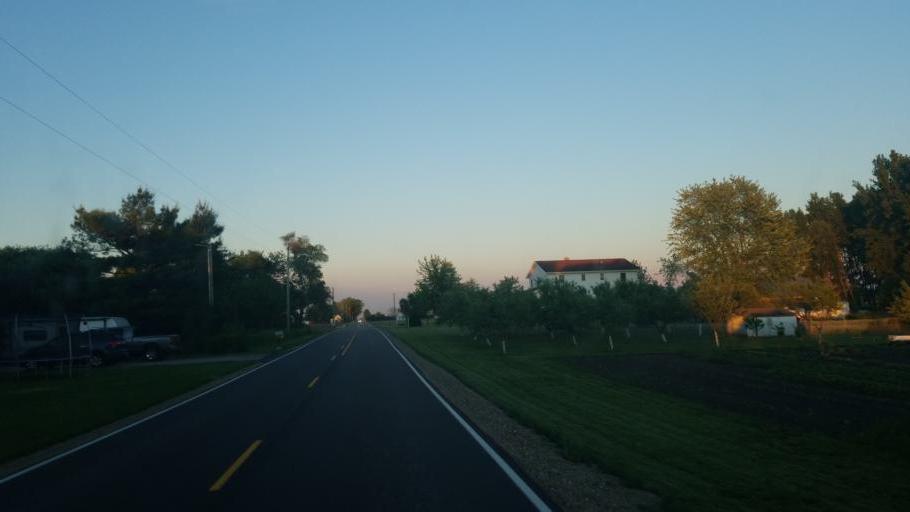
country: US
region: Indiana
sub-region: Elkhart County
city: Nappanee
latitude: 41.3614
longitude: -85.9833
